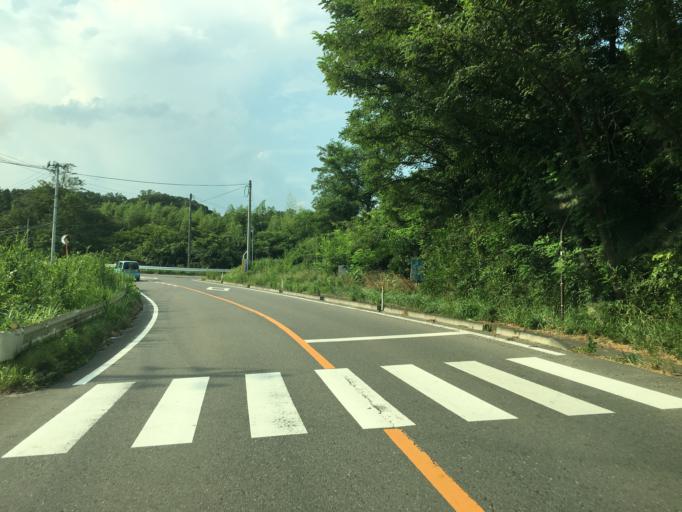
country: JP
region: Fukushima
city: Motomiya
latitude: 37.4672
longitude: 140.4240
